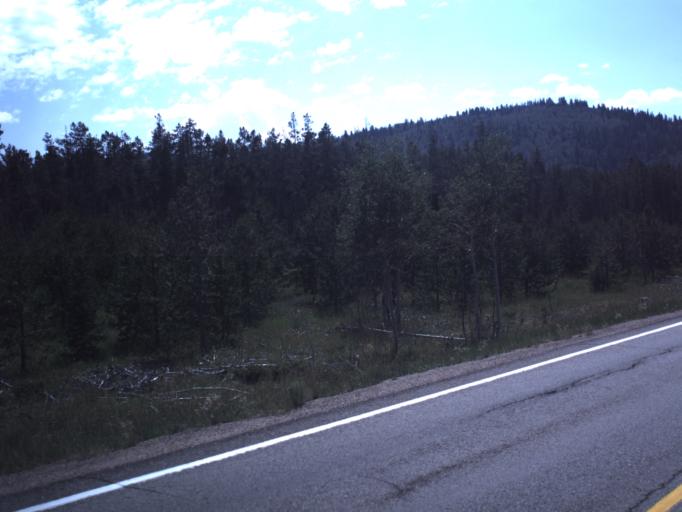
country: US
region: Utah
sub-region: Daggett County
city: Manila
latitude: 40.8267
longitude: -109.4620
